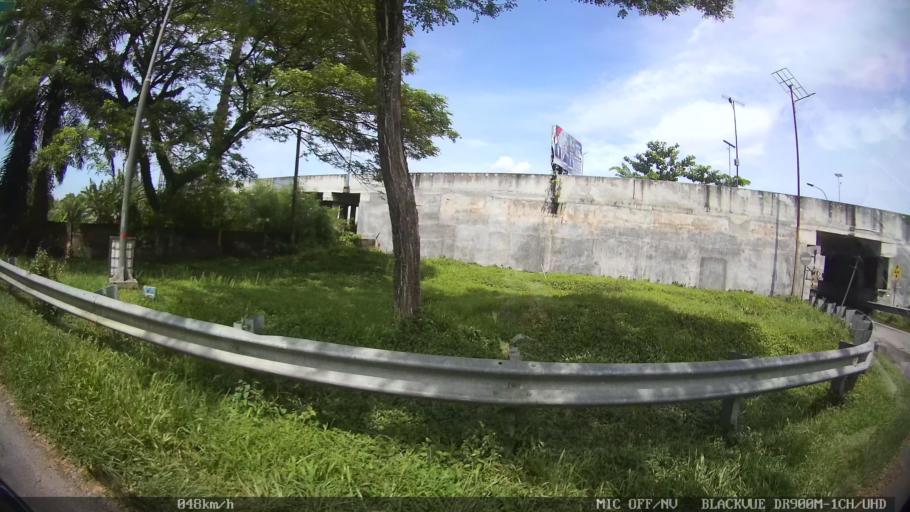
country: ID
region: North Sumatra
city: Percut
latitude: 3.6099
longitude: 98.8548
